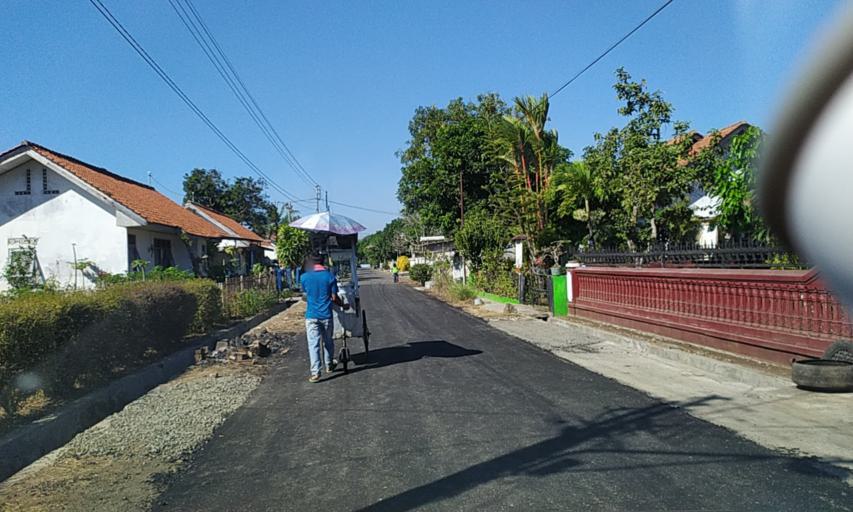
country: ID
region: Central Java
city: Rejanegara
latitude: -7.6920
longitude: 109.0371
